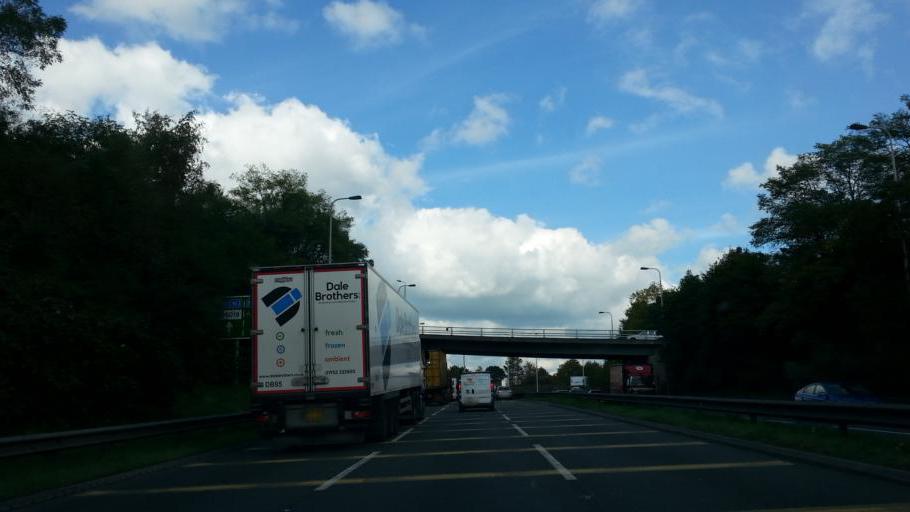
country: GB
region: England
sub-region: Derbyshire
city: Pinxton
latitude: 53.0987
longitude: -1.3260
